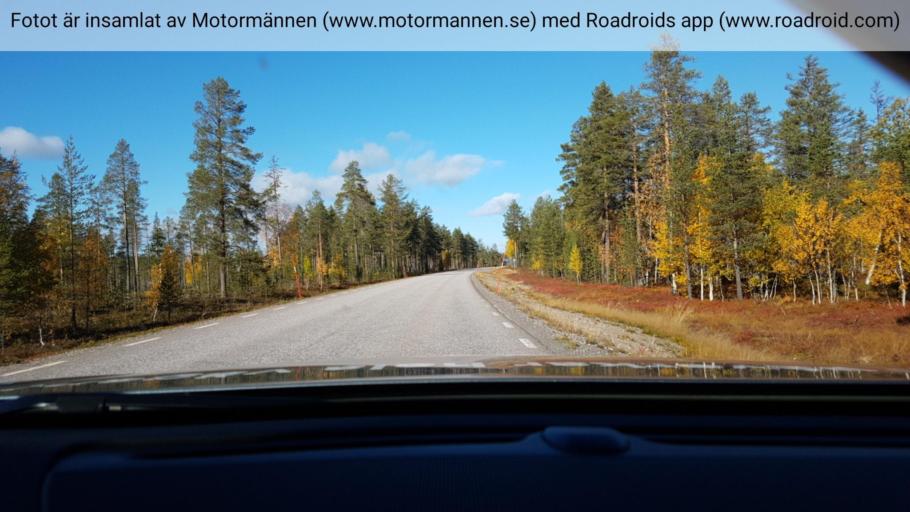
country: SE
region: Norrbotten
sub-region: Arvidsjaurs Kommun
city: Arvidsjaur
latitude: 65.6861
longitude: 18.7937
